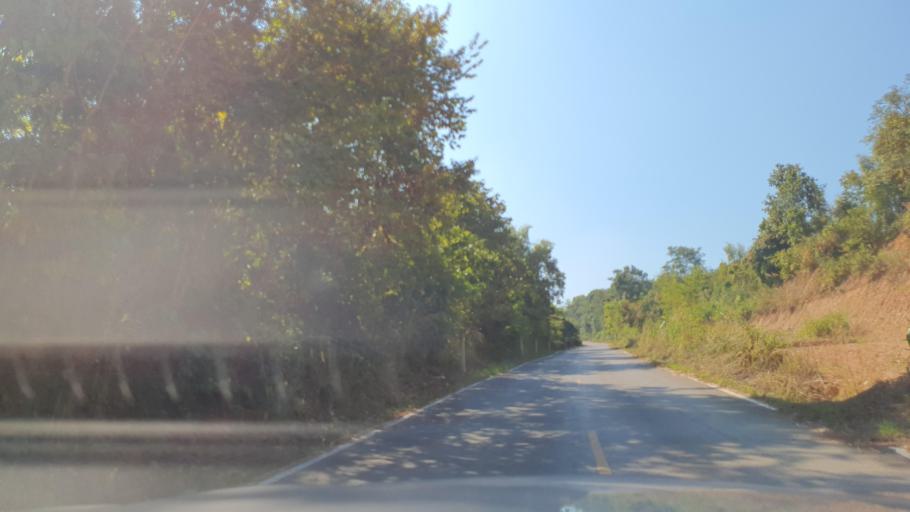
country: TH
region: Nan
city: Pua
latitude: 19.1603
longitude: 100.9067
